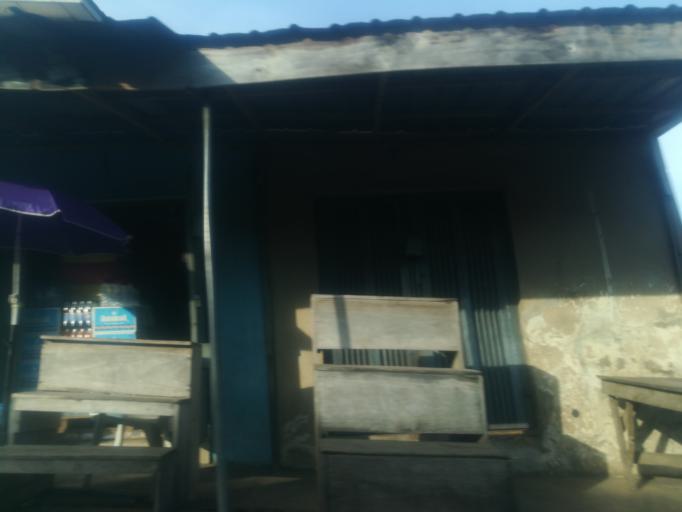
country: NG
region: Oyo
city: Ibadan
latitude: 7.3435
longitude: 3.8874
